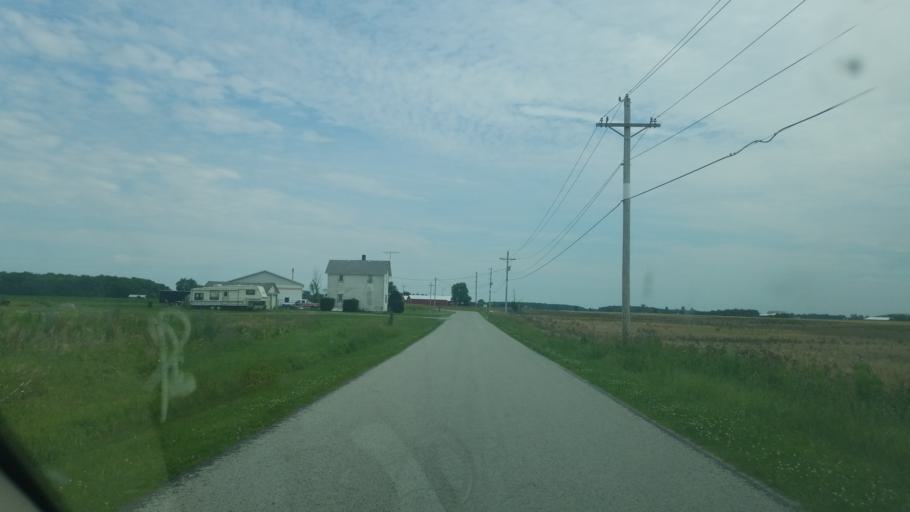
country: US
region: Ohio
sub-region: Seneca County
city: Fostoria
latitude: 41.0557
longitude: -83.4638
